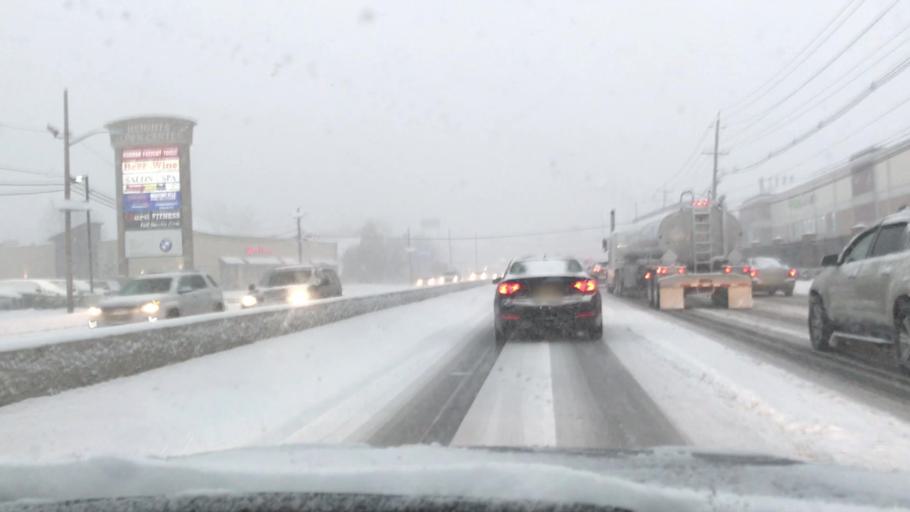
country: US
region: New Jersey
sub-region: Bergen County
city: Hasbrouck Heights
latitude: 40.8513
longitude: -74.0740
